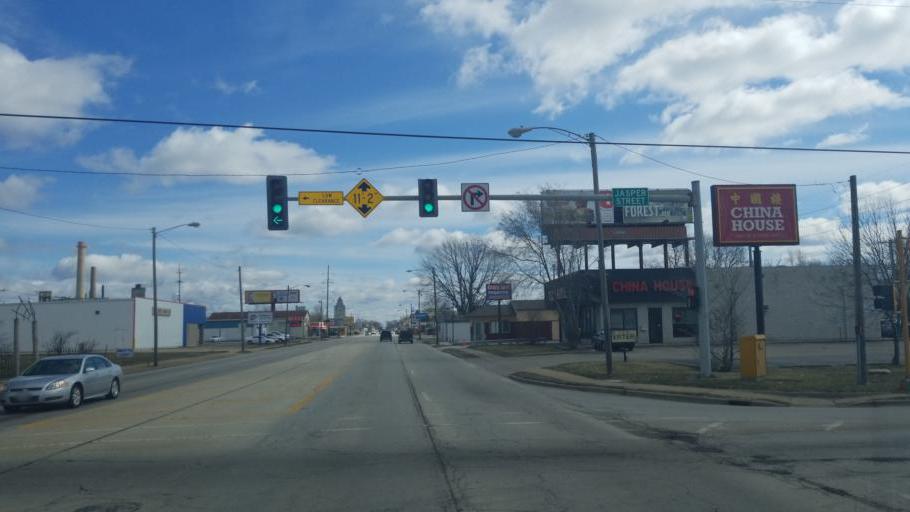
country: US
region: Illinois
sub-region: Macon County
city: Decatur
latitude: 39.8461
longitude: -88.9406
